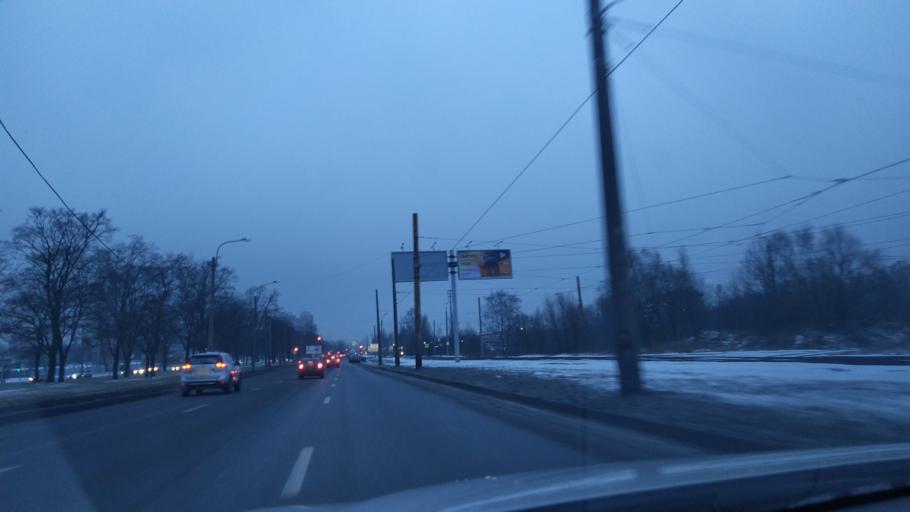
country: RU
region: St.-Petersburg
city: Grazhdanka
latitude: 60.0204
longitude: 30.4326
